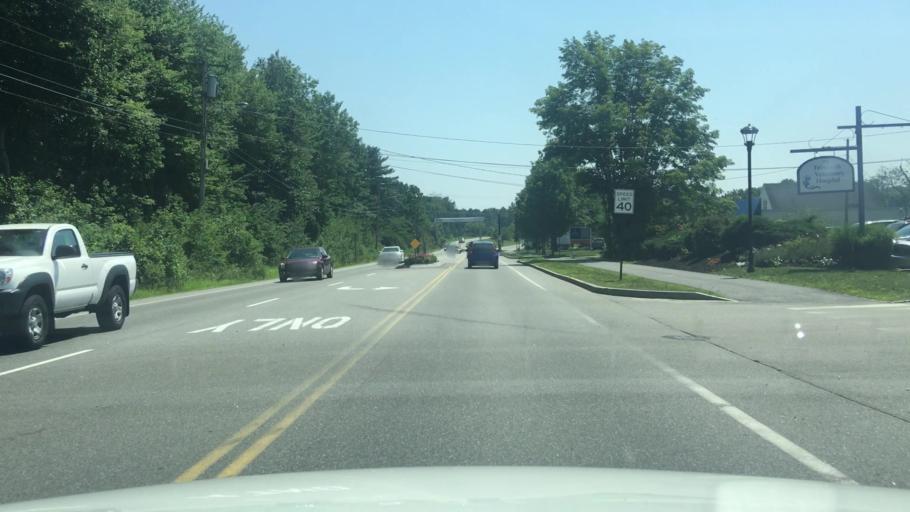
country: US
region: Maine
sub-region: Cumberland County
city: Falmouth
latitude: 43.7143
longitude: -70.2337
